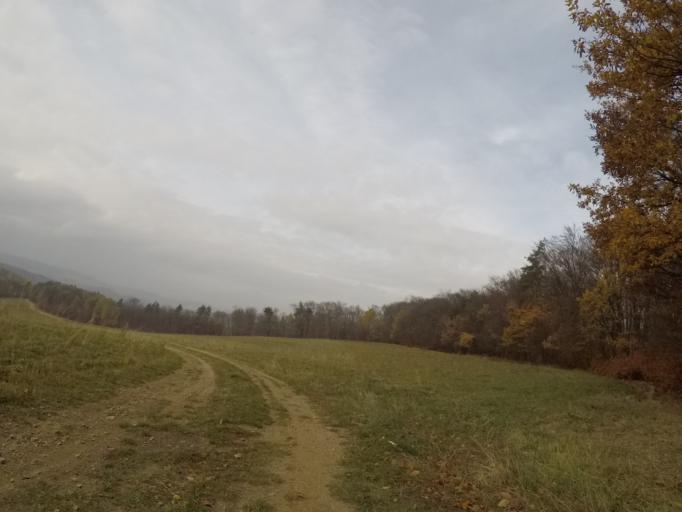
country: SK
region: Presovsky
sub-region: Okres Presov
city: Presov
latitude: 48.9344
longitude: 21.1289
